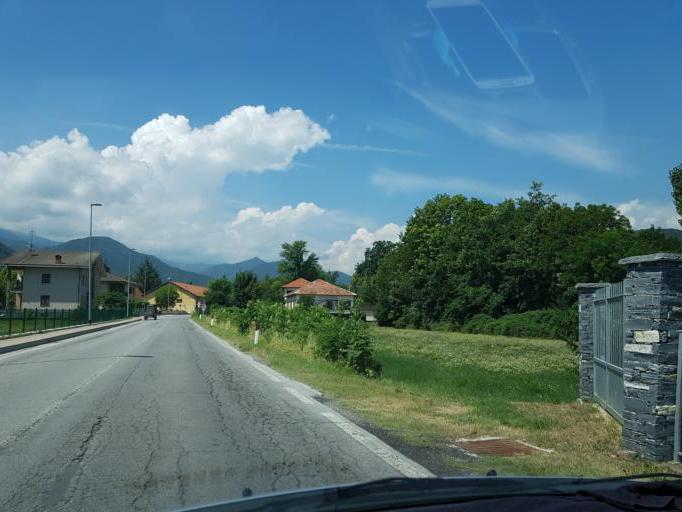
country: IT
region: Piedmont
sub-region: Provincia di Cuneo
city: Tettorosso
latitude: 44.4667
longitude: 7.3442
